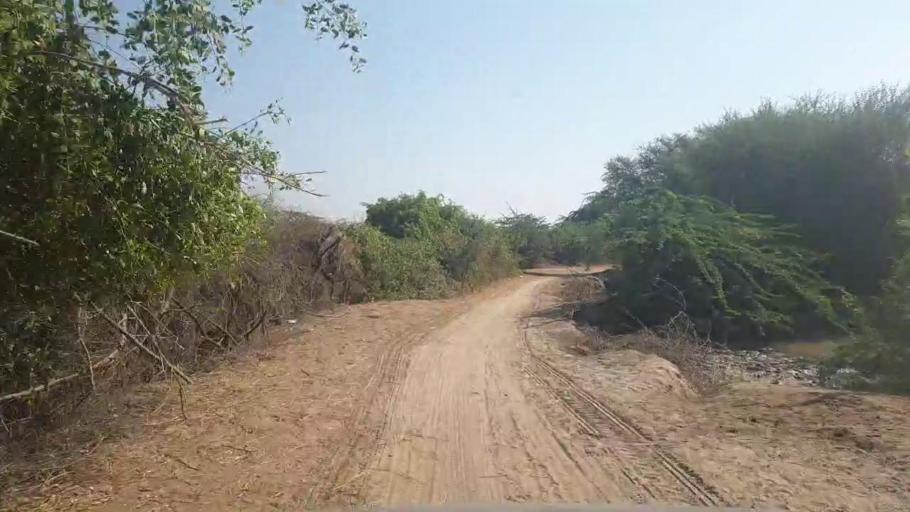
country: PK
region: Sindh
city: Badin
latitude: 24.7155
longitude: 68.8959
